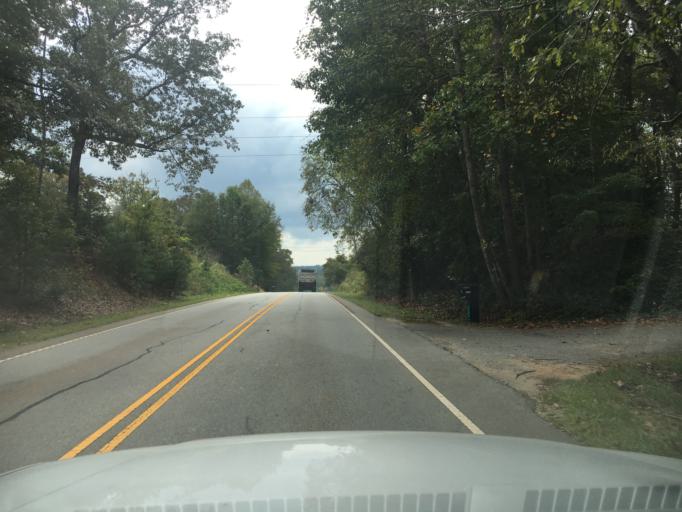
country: US
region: South Carolina
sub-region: Greenville County
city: Greer
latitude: 34.9890
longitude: -82.2455
